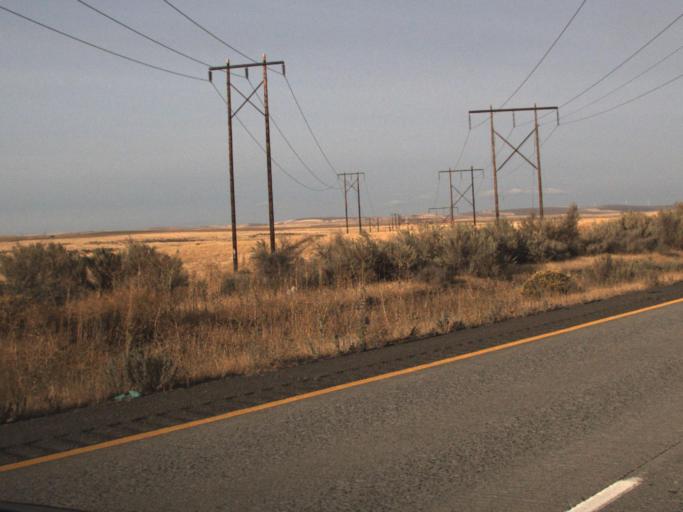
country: US
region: Oregon
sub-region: Umatilla County
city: Umatilla
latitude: 45.9958
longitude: -119.2759
